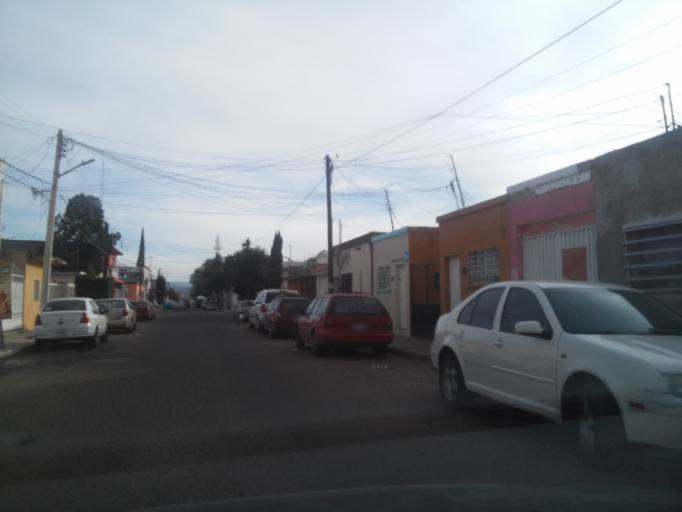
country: MX
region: Durango
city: Victoria de Durango
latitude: 24.0247
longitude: -104.6467
